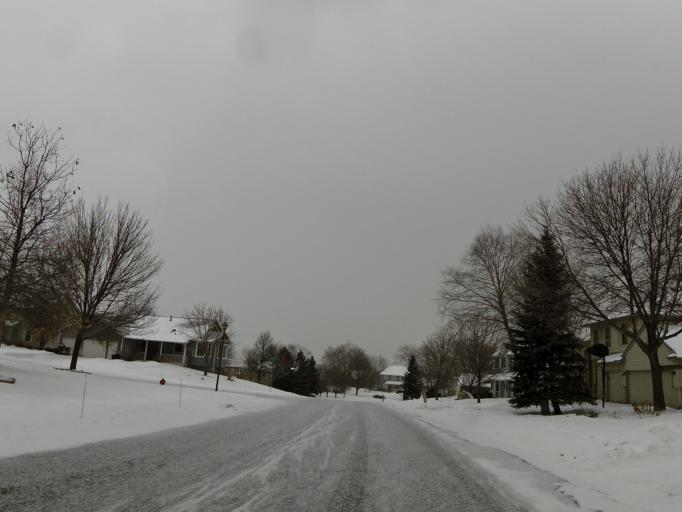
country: US
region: Minnesota
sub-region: Washington County
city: Woodbury
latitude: 44.9330
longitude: -92.9227
